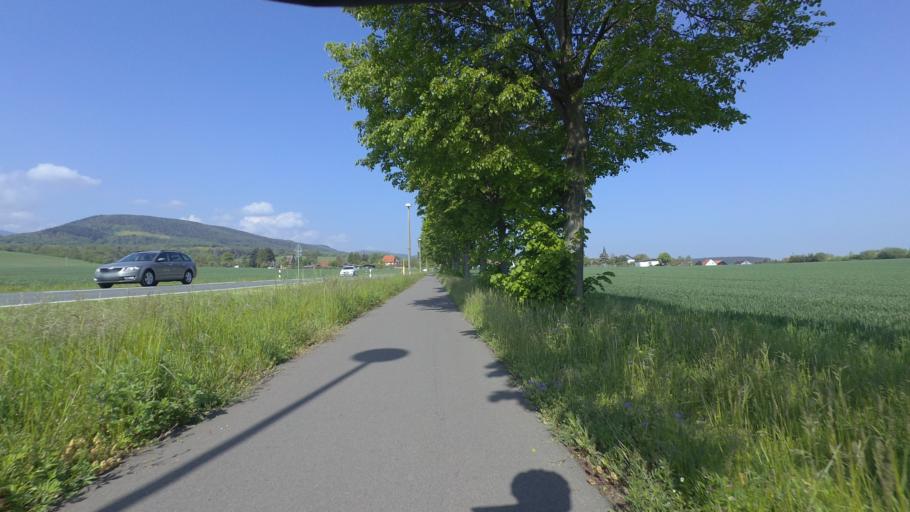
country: DE
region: Saxony-Anhalt
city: Darlingerode
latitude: 51.8538
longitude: 10.7260
